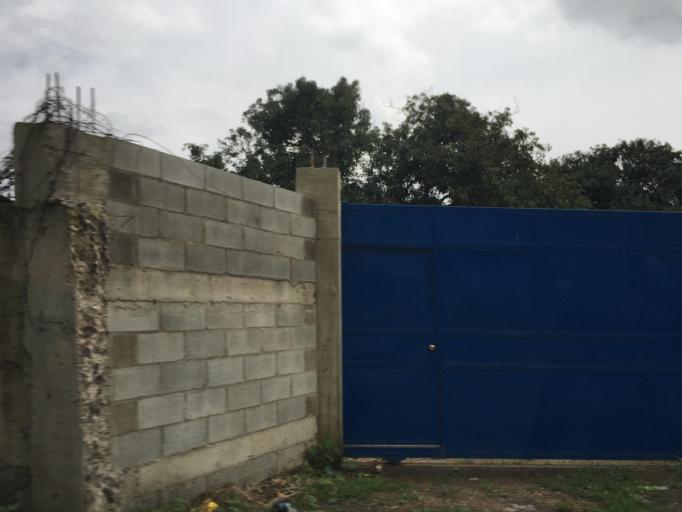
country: GT
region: Guatemala
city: Villa Canales
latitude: 14.4233
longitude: -90.5489
